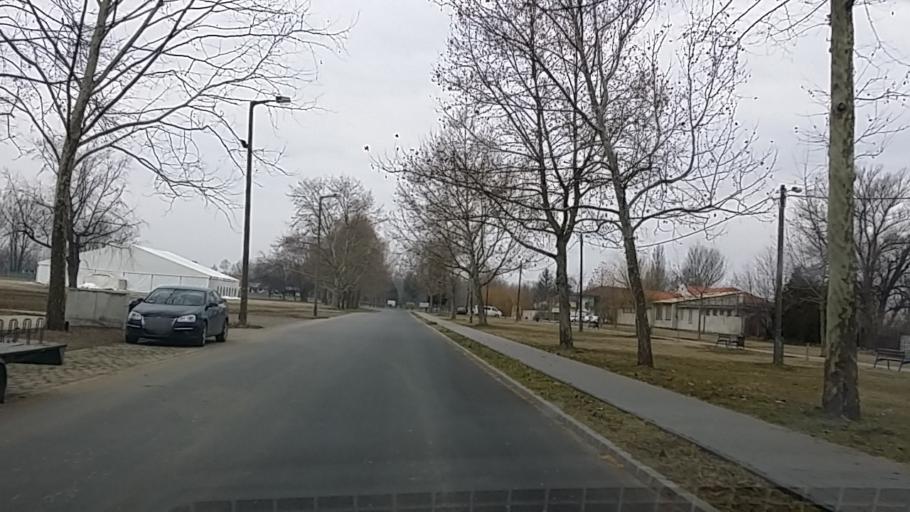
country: HU
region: Bacs-Kiskun
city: Baja
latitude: 46.1777
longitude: 18.9450
